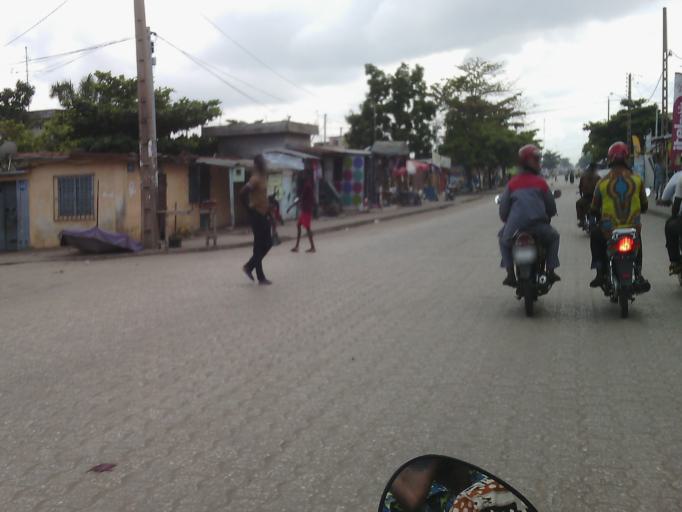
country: BJ
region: Littoral
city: Cotonou
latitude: 6.3714
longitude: 2.4166
